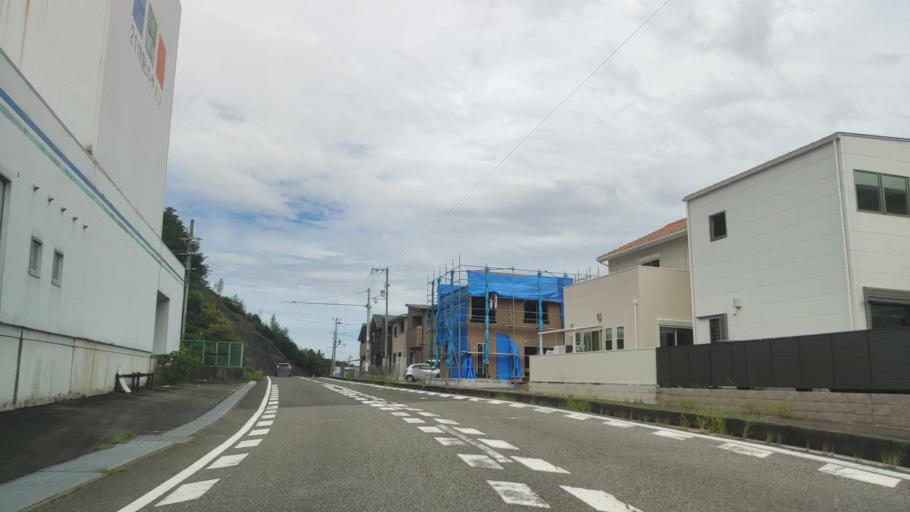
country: JP
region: Wakayama
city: Tanabe
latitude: 33.6873
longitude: 135.3891
